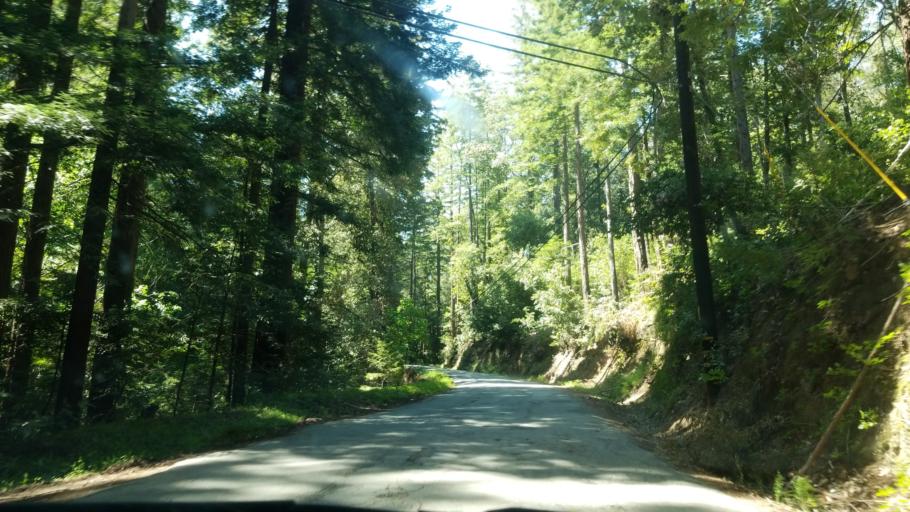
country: US
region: California
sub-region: Santa Cruz County
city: Day Valley
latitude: 37.0585
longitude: -121.8216
